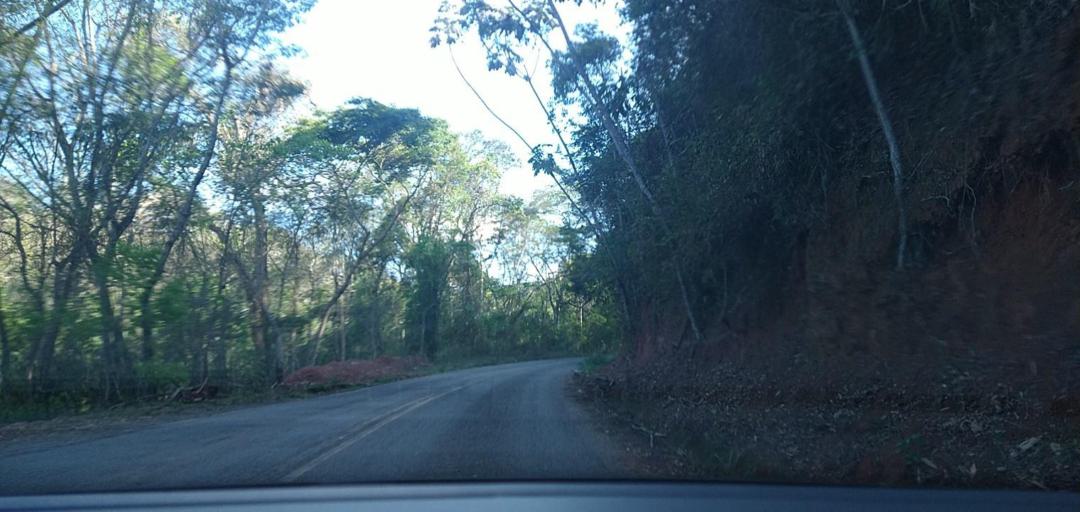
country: BR
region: Minas Gerais
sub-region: Alvinopolis
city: Alvinopolis
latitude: -20.1714
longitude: -42.9210
